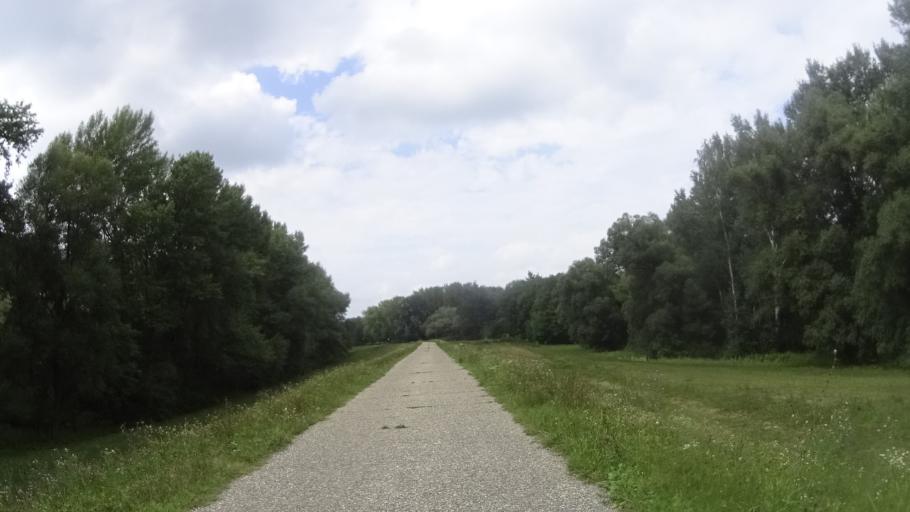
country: SK
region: Trnavsky
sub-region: Okres Dunajska Streda
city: Velky Meder
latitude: 47.7622
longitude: 17.7328
